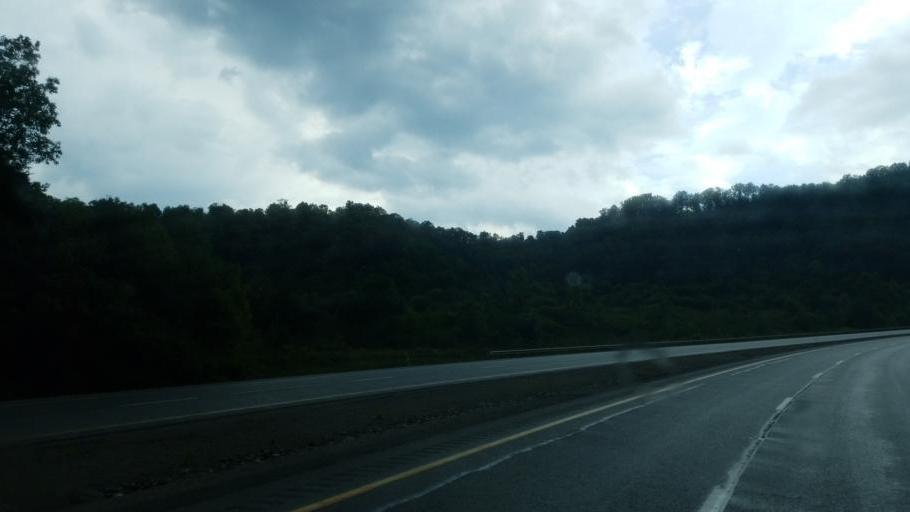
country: US
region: Kentucky
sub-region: Pike County
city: Pikeville
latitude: 37.5183
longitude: -82.4580
